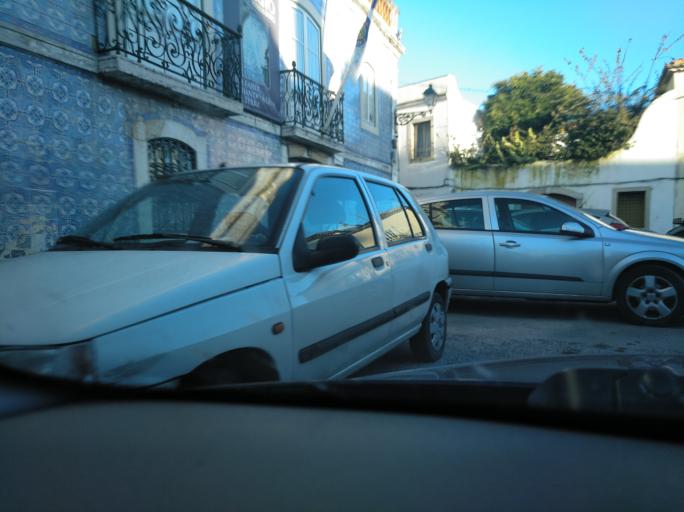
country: PT
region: Lisbon
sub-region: Odivelas
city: Olival do Basto
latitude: 38.7732
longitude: -9.1734
